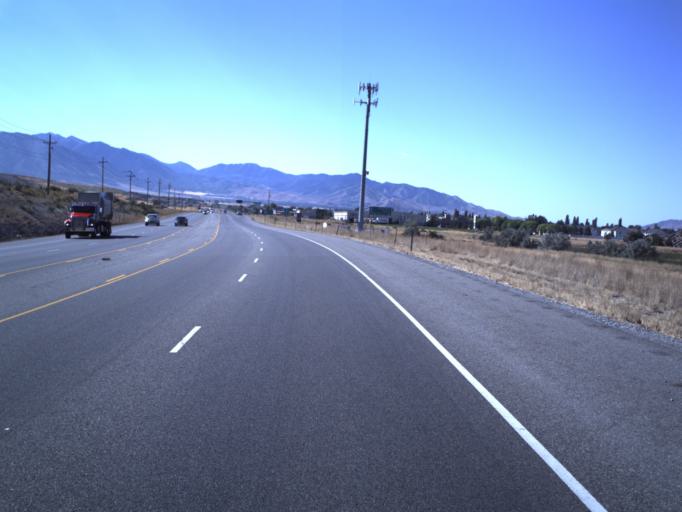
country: US
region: Utah
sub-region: Tooele County
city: Stansbury park
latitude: 40.6583
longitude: -112.2899
